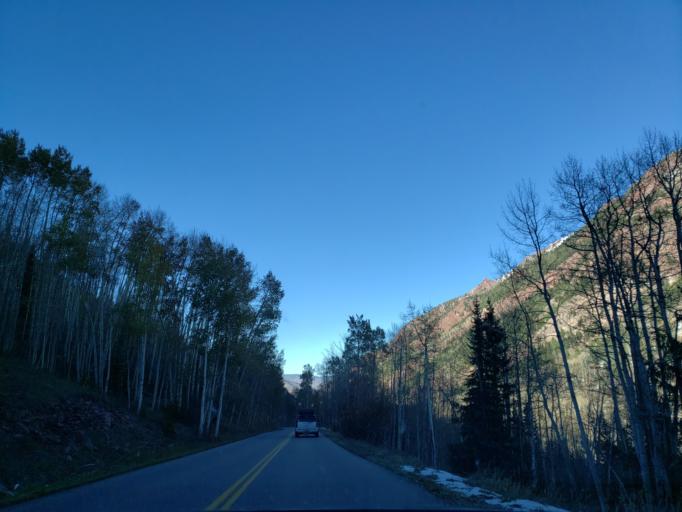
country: US
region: Colorado
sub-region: Pitkin County
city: Snowmass Village
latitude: 39.1136
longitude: -106.9123
